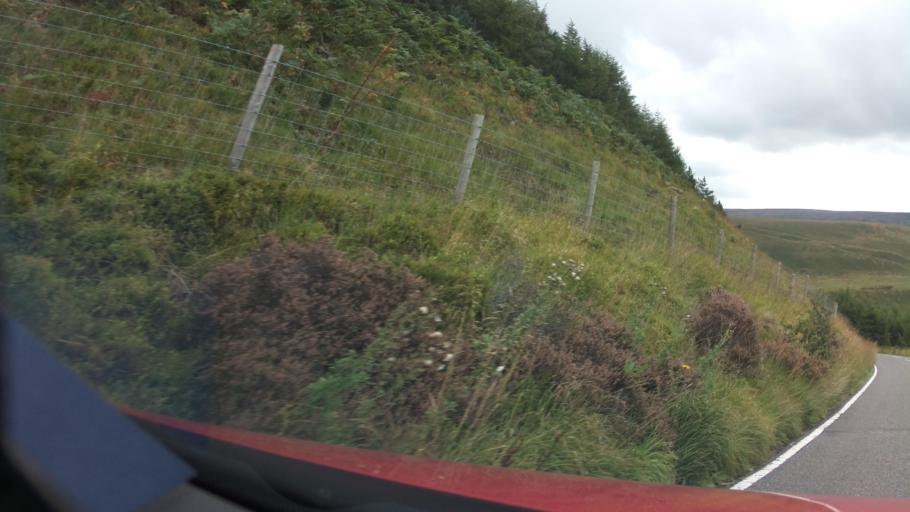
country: GB
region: England
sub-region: Kirklees
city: Meltham
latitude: 53.5083
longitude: -1.8534
